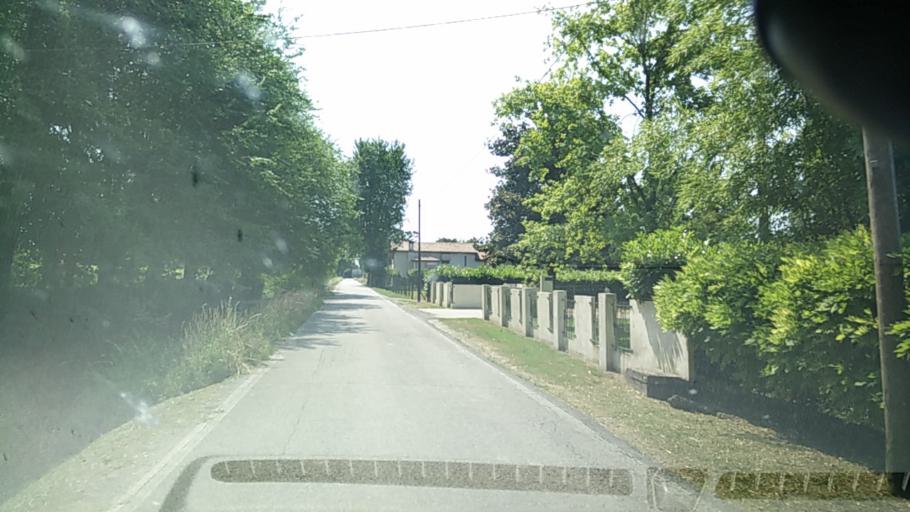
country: IT
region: Veneto
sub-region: Provincia di Treviso
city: Lutrano
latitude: 45.8146
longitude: 12.4671
